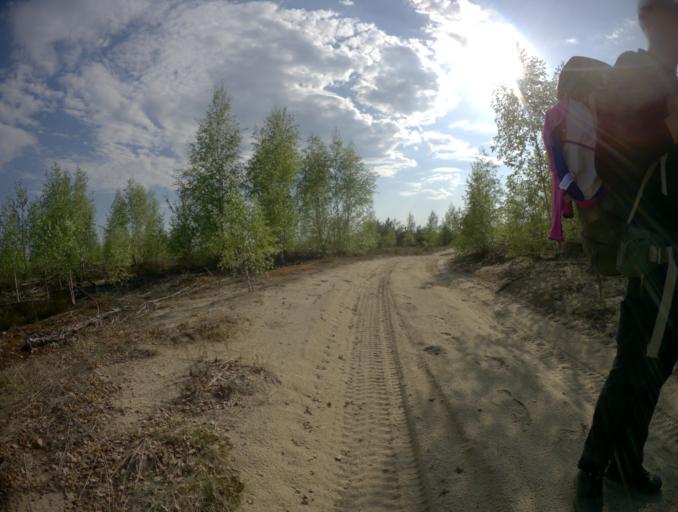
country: RU
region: Ivanovo
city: Talitsy
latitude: 56.4120
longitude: 42.2494
